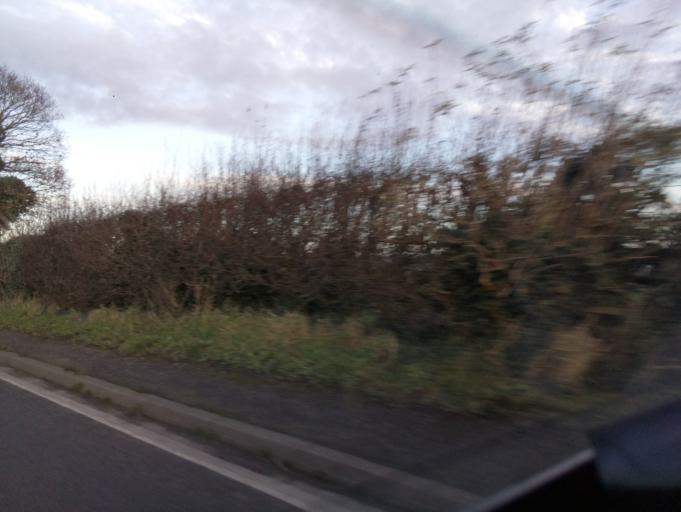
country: GB
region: England
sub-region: Staffordshire
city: Stone
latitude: 52.8652
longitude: -2.1312
